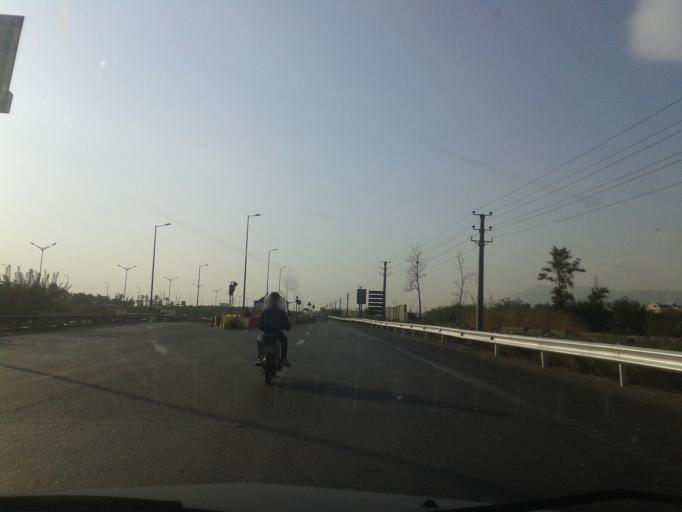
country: IR
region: Tehran
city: Eslamshahr
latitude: 35.6564
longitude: 51.2584
